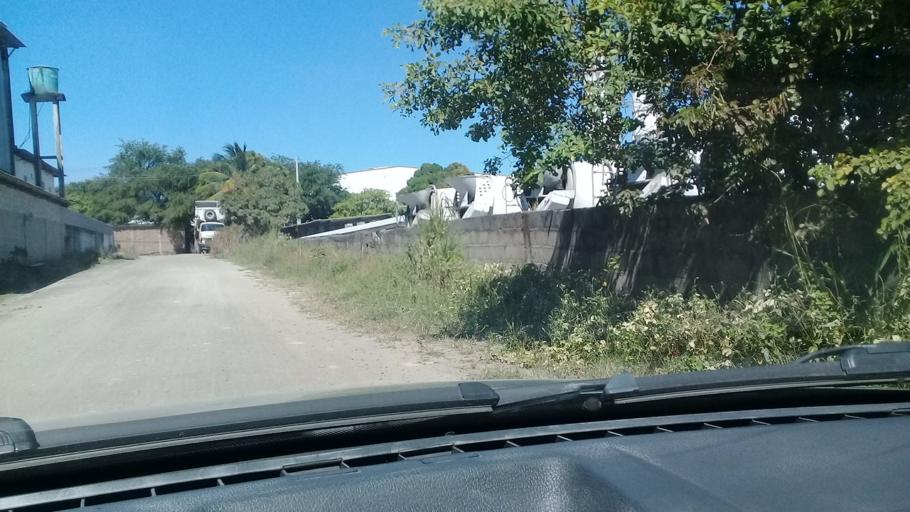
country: BR
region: Pernambuco
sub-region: Jaboatao Dos Guararapes
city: Jaboatao
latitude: -8.1535
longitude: -34.9504
